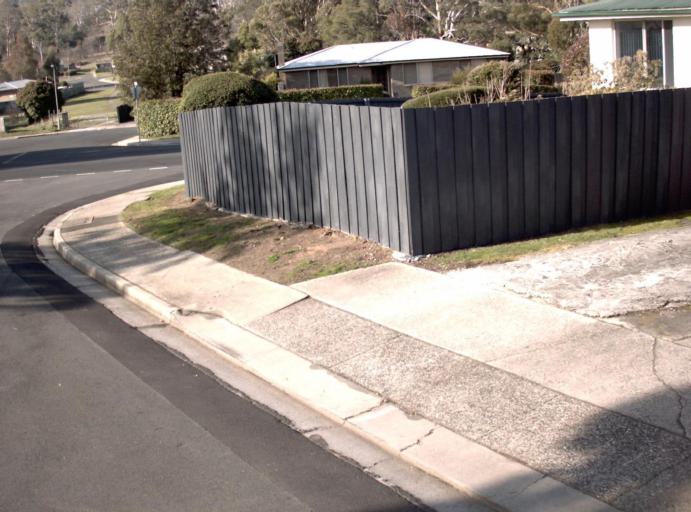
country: AU
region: Tasmania
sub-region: Launceston
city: Newstead
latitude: -41.4126
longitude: 147.1696
